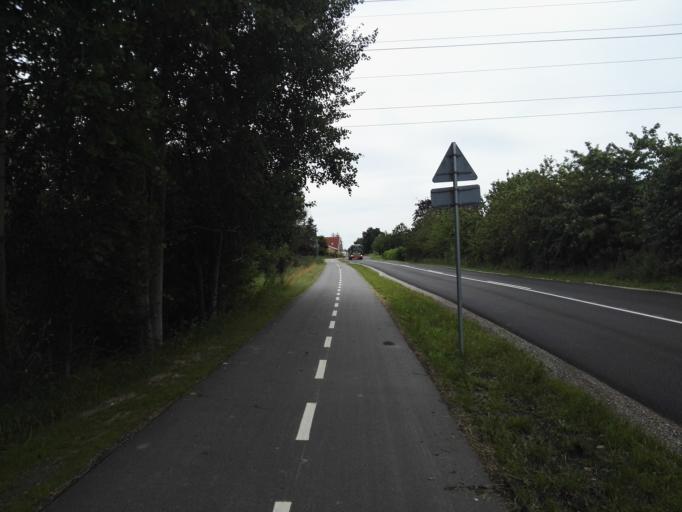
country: DK
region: Capital Region
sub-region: Hillerod Kommune
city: Skaevinge
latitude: 55.9142
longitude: 12.1715
